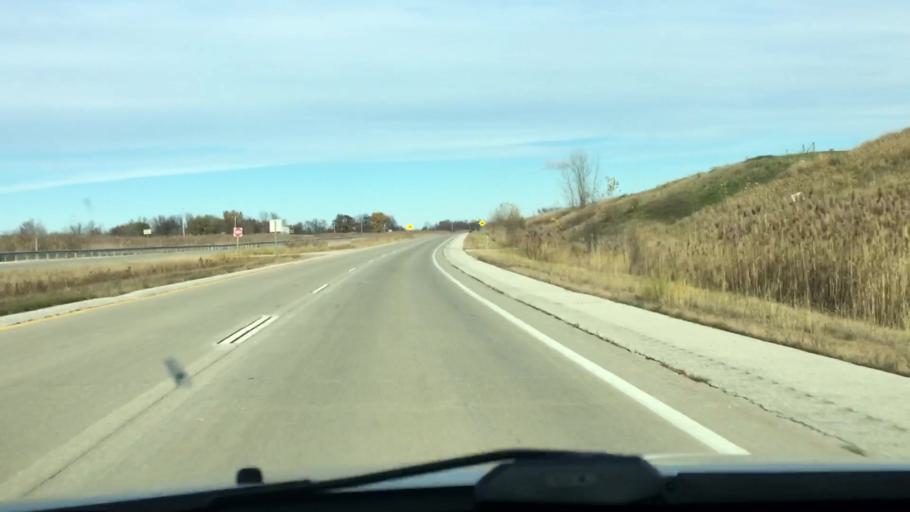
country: US
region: Wisconsin
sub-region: Kewaunee County
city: Luxemburg
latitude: 44.6679
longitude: -87.7416
